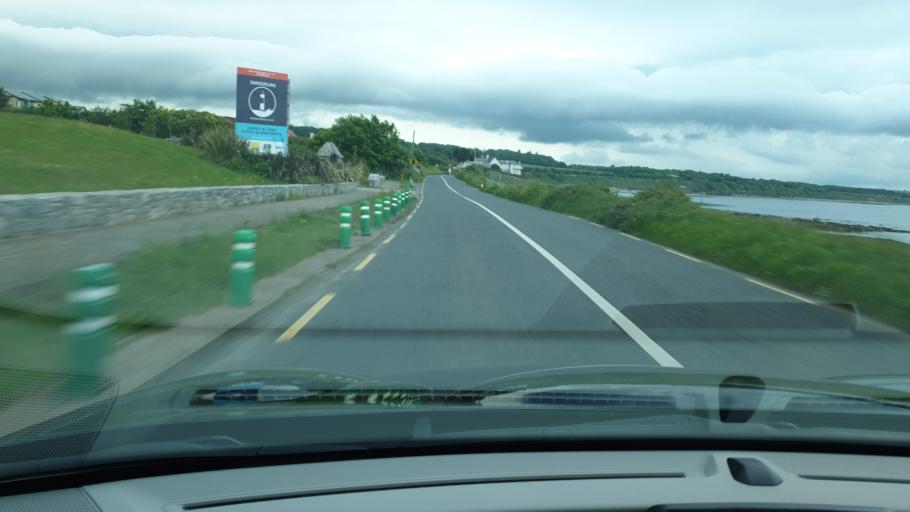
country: IE
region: Leinster
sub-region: Fingal County
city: Skerries
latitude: 53.5863
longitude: -6.1353
